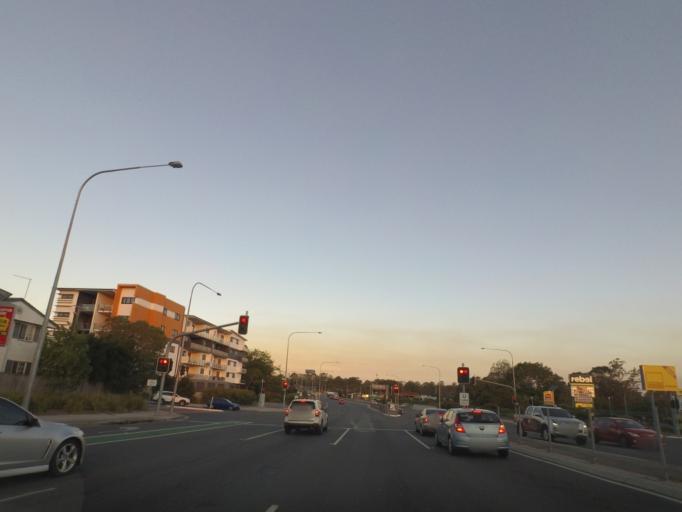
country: AU
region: Queensland
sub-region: Brisbane
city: Nathan
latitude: -27.5618
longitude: 153.0722
